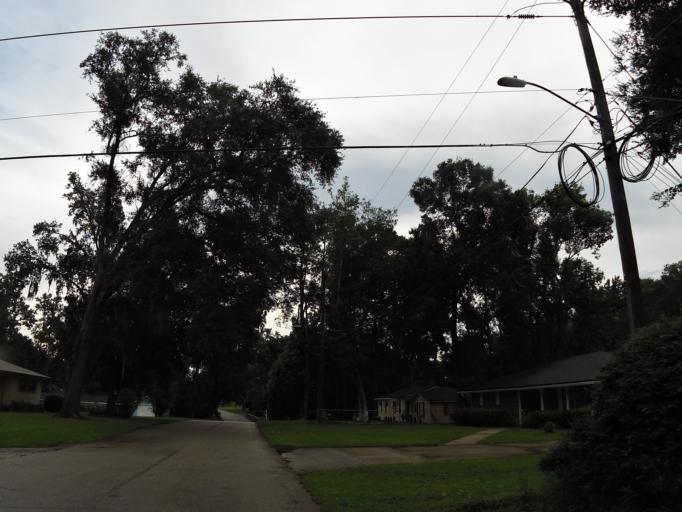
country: US
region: Florida
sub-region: Duval County
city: Jacksonville
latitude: 30.2993
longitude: -81.5991
